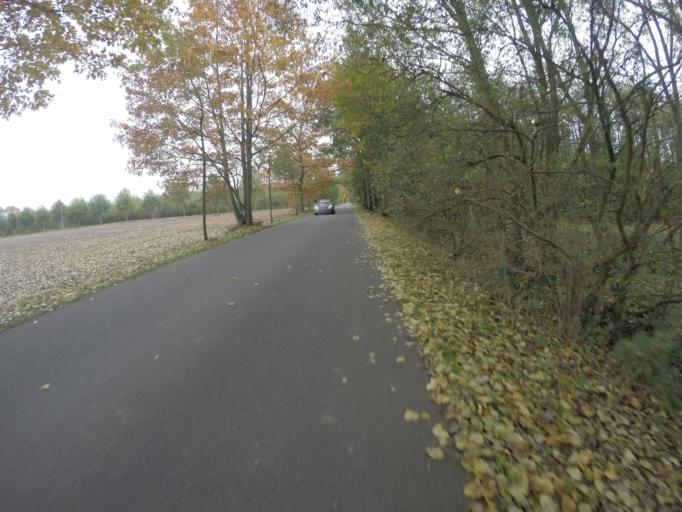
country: BE
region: Flanders
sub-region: Provincie Oost-Vlaanderen
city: Knesselare
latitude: 51.1640
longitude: 3.4221
